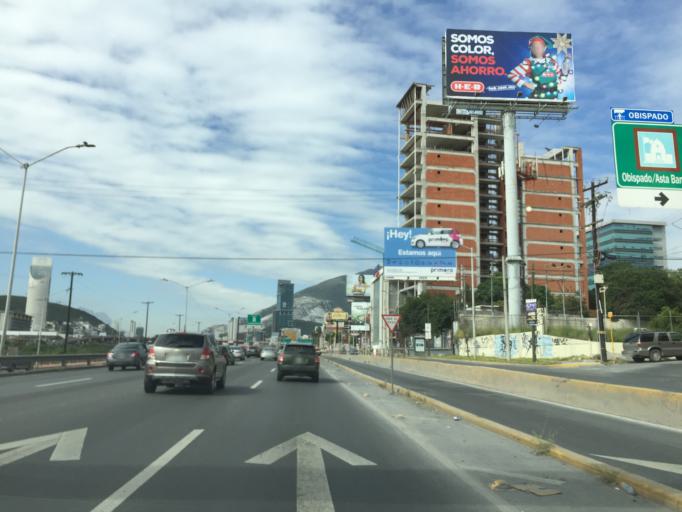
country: MX
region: Nuevo Leon
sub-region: Monterrey
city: Monterrey
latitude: 25.6701
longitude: -100.3442
